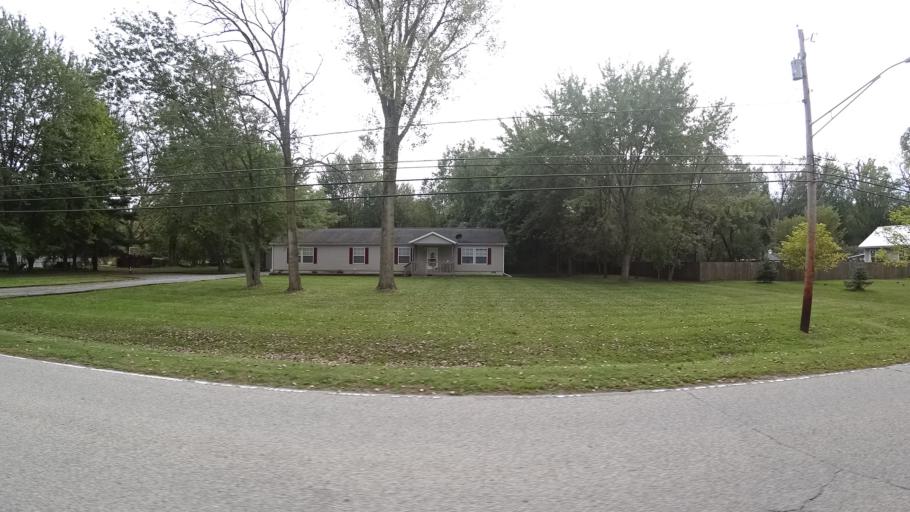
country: US
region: Indiana
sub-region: LaPorte County
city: Long Beach
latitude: 41.7381
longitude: -86.8171
